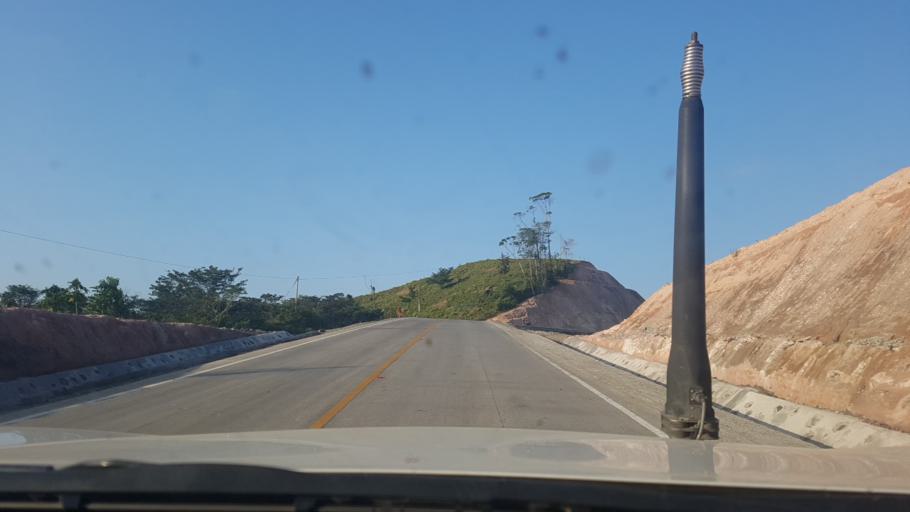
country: NI
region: Atlantico Sur
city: Rama
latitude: 11.8295
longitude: -84.0811
